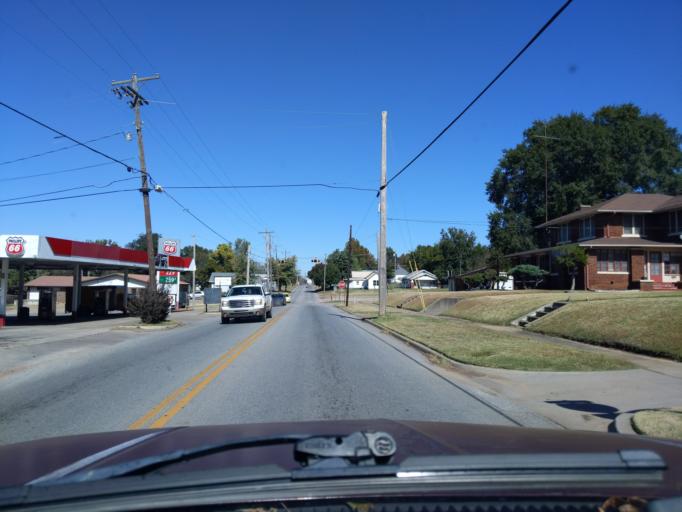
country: US
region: Oklahoma
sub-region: Creek County
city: Bristow
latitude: 35.8277
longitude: -96.3872
